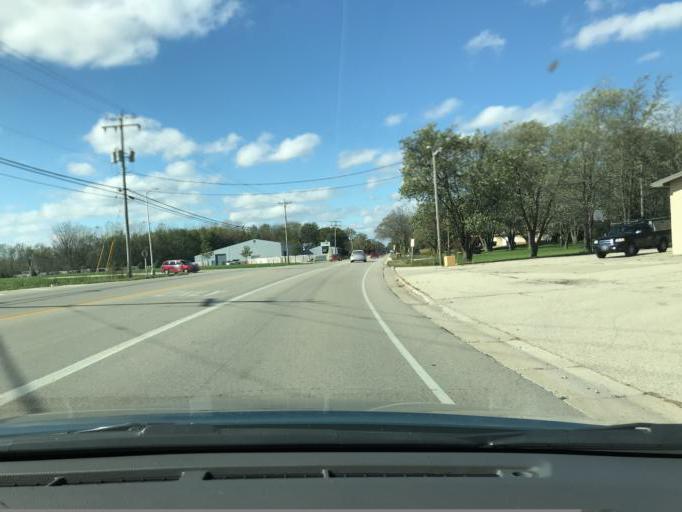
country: US
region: Wisconsin
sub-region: Kenosha County
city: Somers
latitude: 42.6043
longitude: -87.9264
